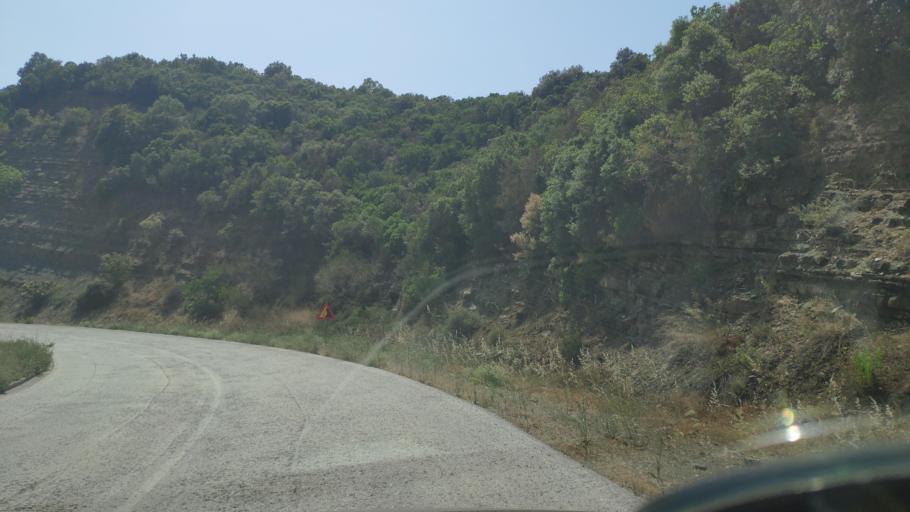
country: GR
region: Epirus
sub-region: Nomos Artas
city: Peta
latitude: 39.1817
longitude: 21.0924
